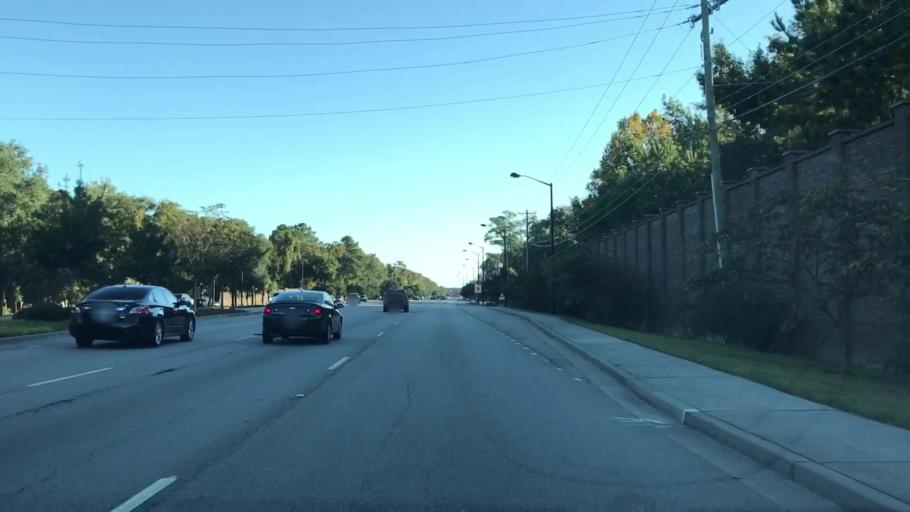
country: US
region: South Carolina
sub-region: Charleston County
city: Isle of Palms
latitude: 32.8355
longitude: -79.8235
